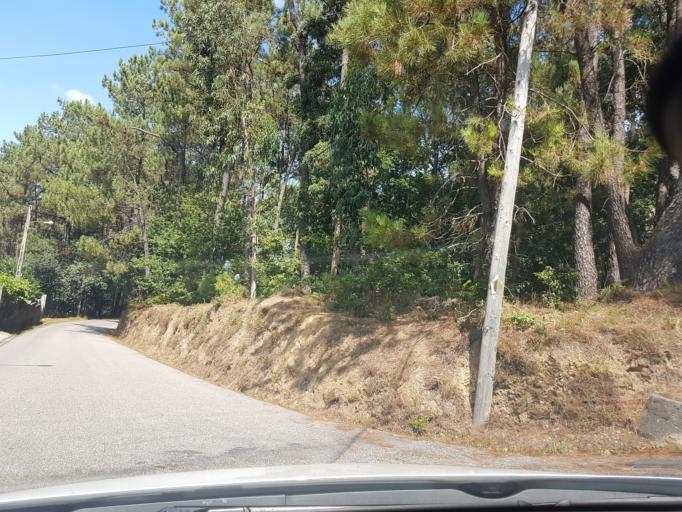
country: ES
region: Galicia
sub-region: Provincia de Pontevedra
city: Porrino
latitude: 42.1943
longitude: -8.6221
